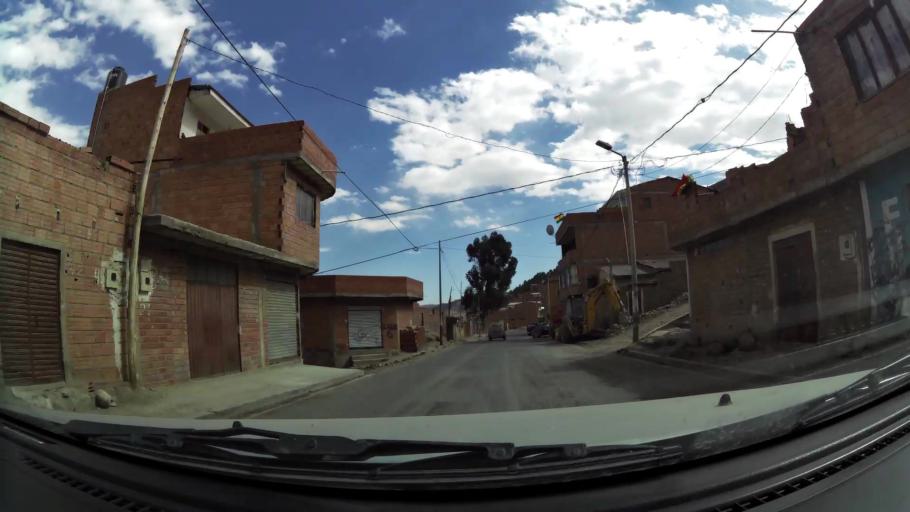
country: BO
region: La Paz
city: La Paz
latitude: -16.4596
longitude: -68.1040
